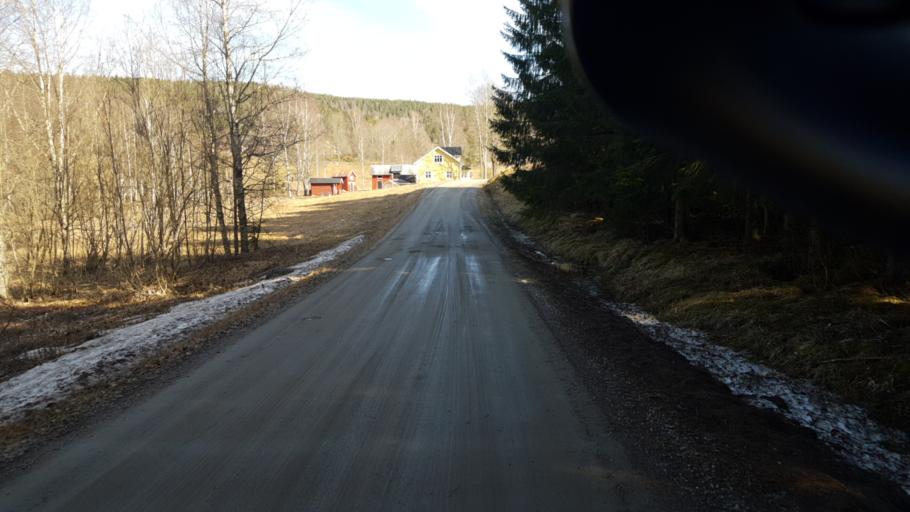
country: SE
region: Vaermland
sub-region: Arvika Kommun
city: Arvika
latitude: 59.6886
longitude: 12.7789
